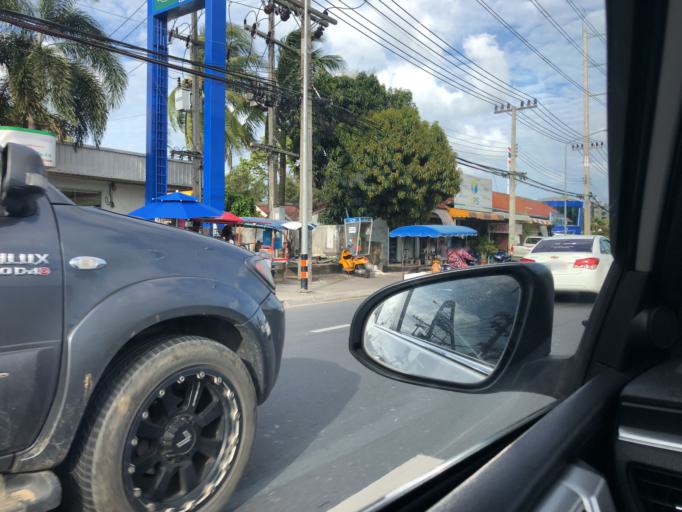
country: TH
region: Phuket
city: Ban Ko Kaeo
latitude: 7.9581
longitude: 98.3852
